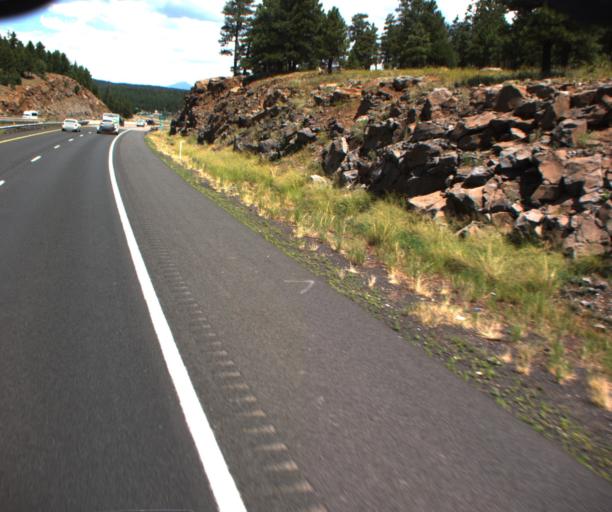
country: US
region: Arizona
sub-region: Coconino County
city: Sedona
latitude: 34.9312
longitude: -111.6491
